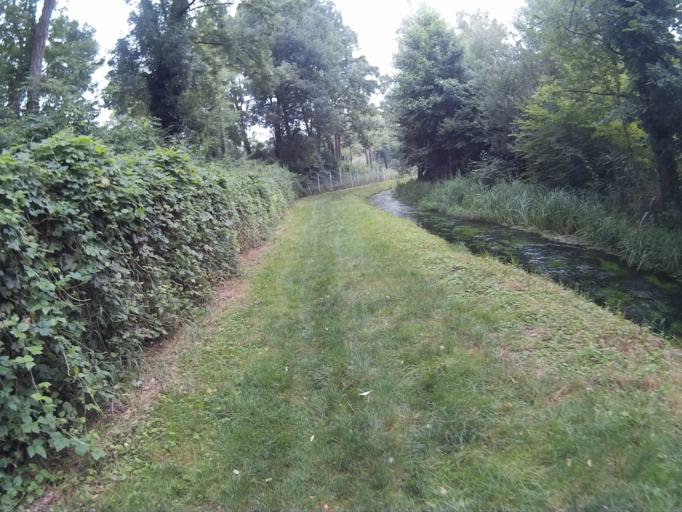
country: HU
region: Veszprem
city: Papa
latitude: 47.2835
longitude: 17.5173
